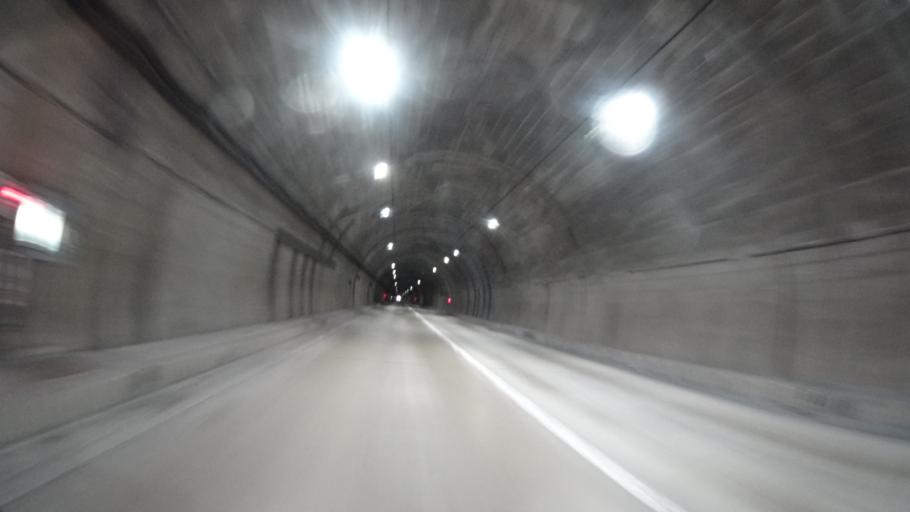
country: JP
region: Fukui
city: Maruoka
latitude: 36.1261
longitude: 136.3230
